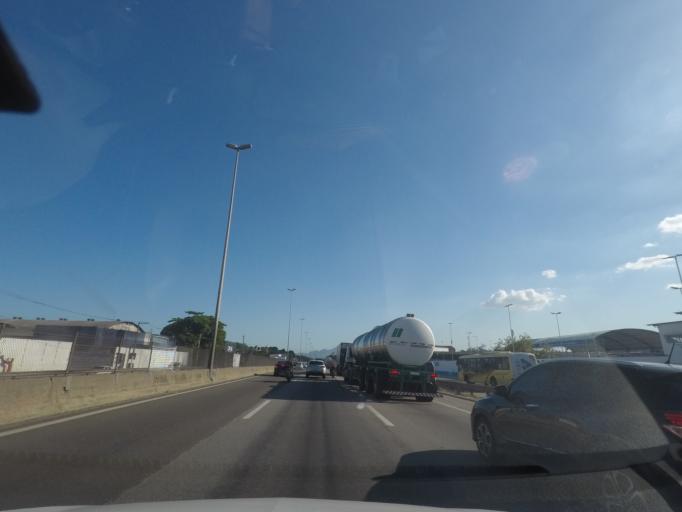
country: BR
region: Rio de Janeiro
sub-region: Duque De Caxias
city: Duque de Caxias
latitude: -22.7529
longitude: -43.2875
